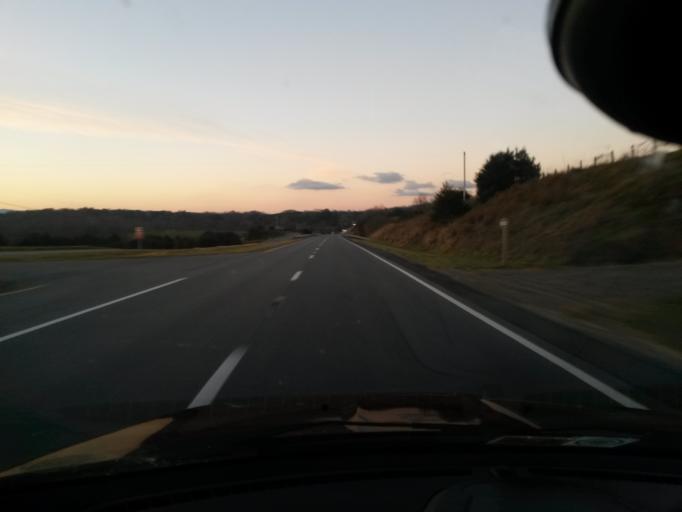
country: US
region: Virginia
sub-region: Botetourt County
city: Fincastle
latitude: 37.5755
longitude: -79.8353
